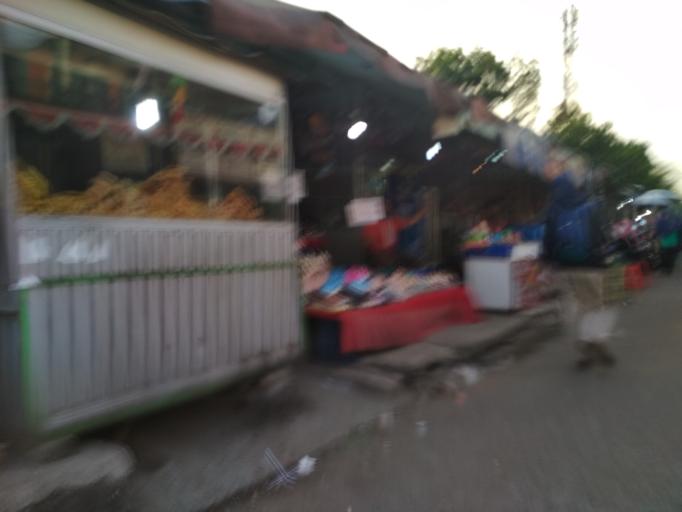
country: ID
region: West Java
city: Ciampea
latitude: -6.5621
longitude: 106.7319
